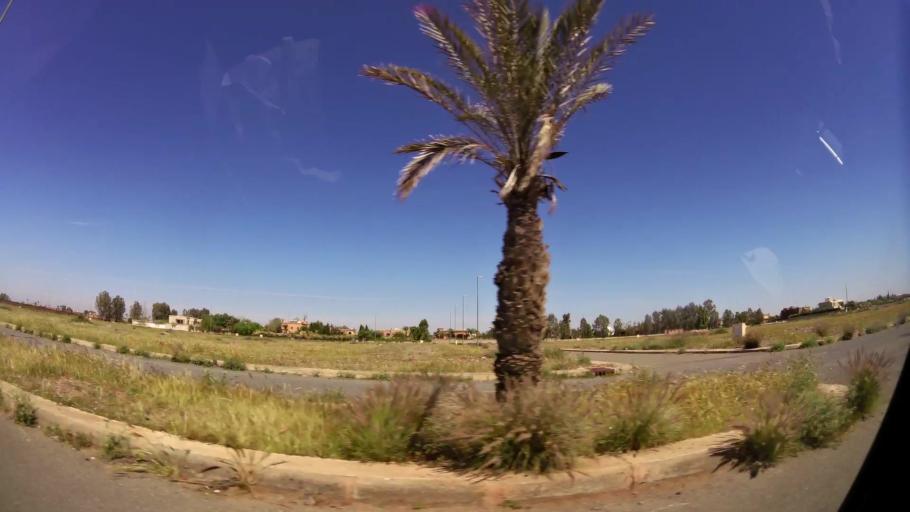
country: MA
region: Marrakech-Tensift-Al Haouz
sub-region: Marrakech
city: Marrakesh
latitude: 31.5852
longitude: -8.0025
